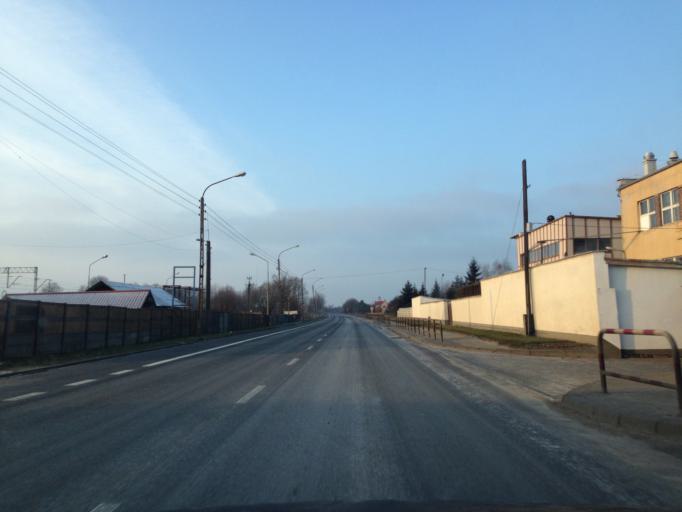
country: PL
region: Greater Poland Voivodeship
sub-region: Powiat poznanski
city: Pobiedziska
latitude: 52.4792
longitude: 17.2744
